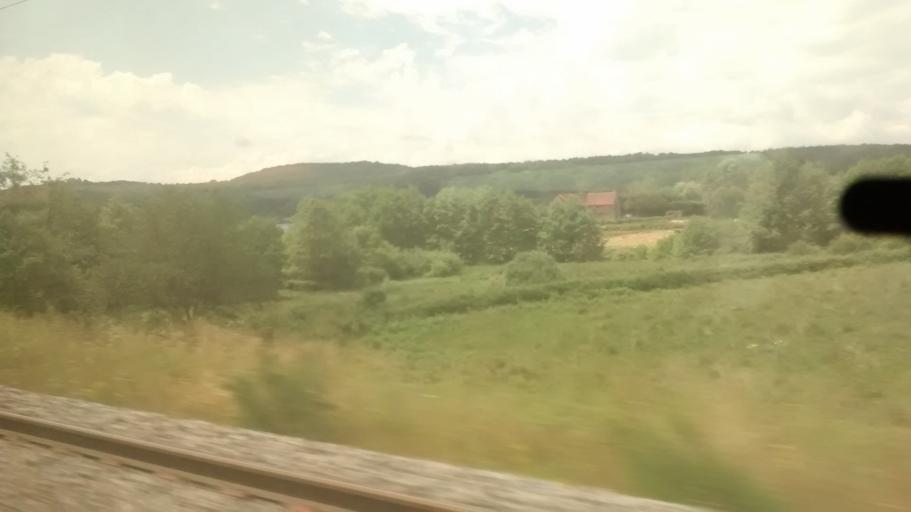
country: FR
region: Bourgogne
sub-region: Departement de Saone-et-Loire
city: Le Breuil
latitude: 46.8678
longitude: 4.4932
